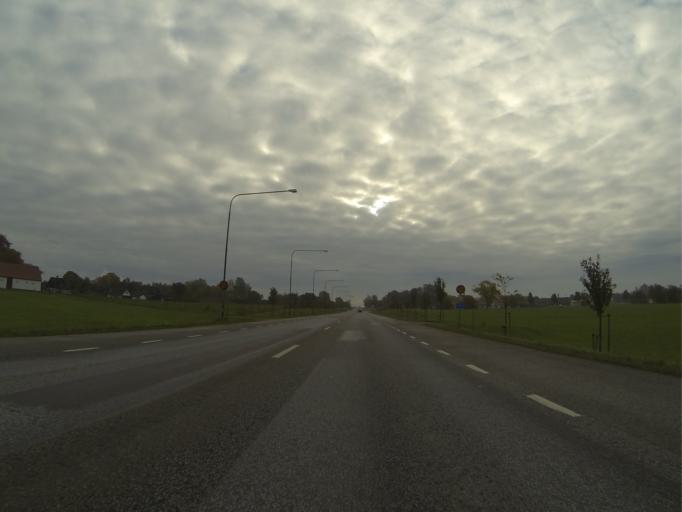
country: SE
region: Skane
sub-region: Tomelilla Kommun
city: Tomelilla
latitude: 55.5532
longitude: 13.9363
